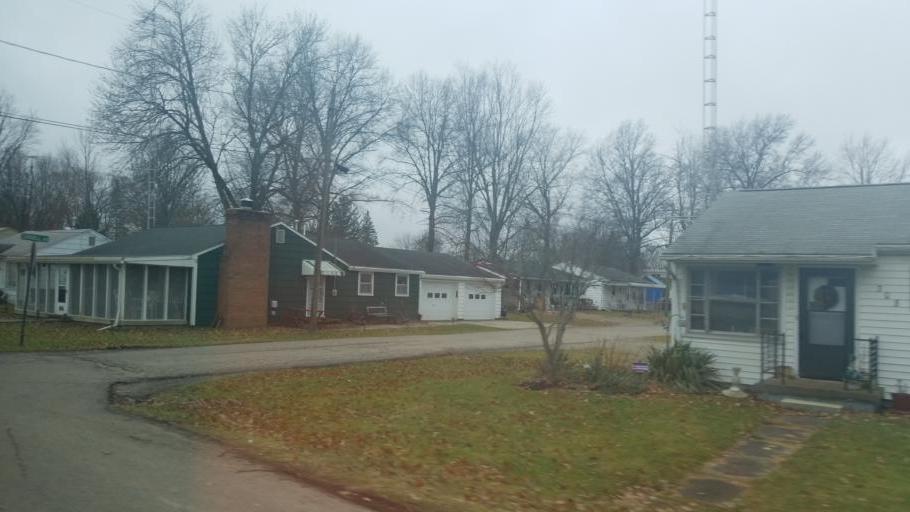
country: US
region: Ohio
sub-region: Crawford County
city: Galion
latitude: 40.7302
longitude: -82.7694
